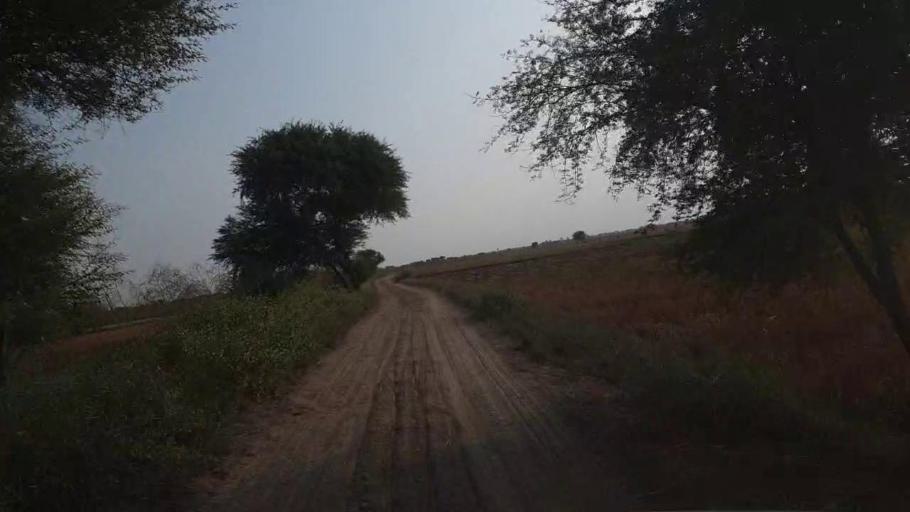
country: PK
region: Sindh
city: Matli
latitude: 25.0414
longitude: 68.7490
